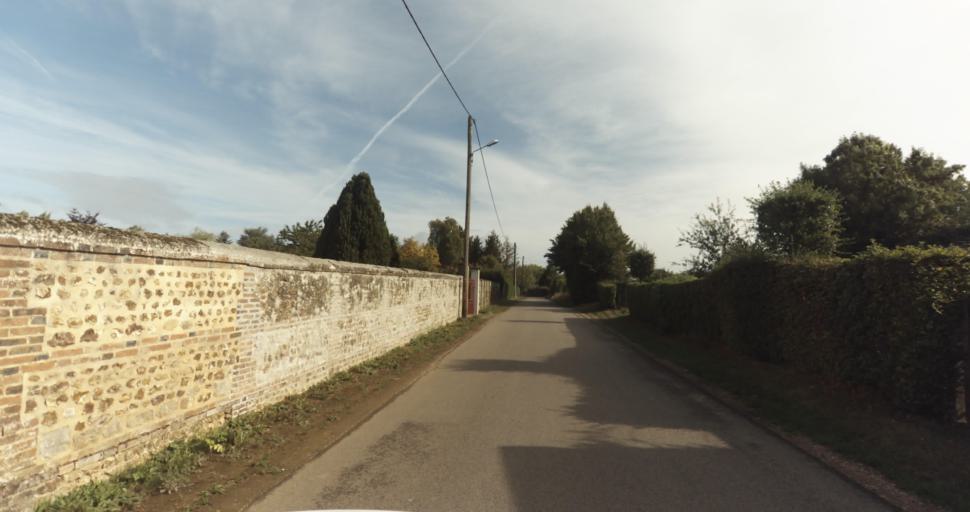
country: FR
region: Lower Normandy
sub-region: Departement de l'Orne
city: Gace
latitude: 48.8950
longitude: 0.3407
